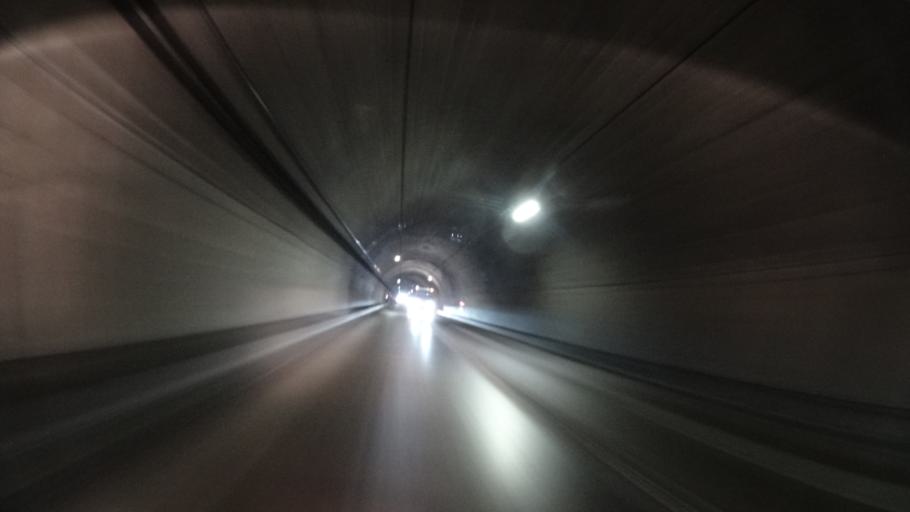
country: JP
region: Fukui
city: Maruoka
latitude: 36.1324
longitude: 136.3241
